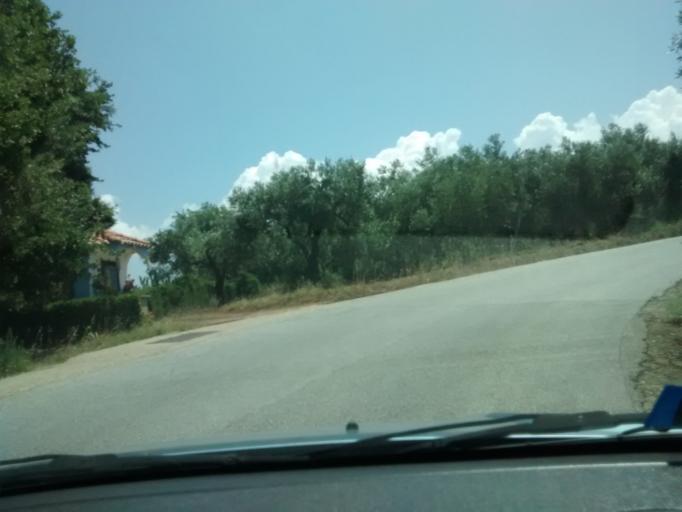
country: IT
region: Calabria
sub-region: Provincia di Catanzaro
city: Maida
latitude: 38.8984
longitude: 16.3936
